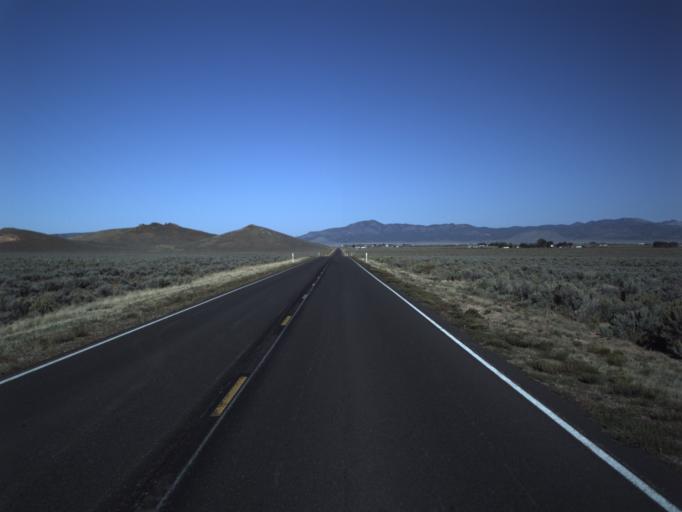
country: US
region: Utah
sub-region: Washington County
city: Enterprise
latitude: 37.7363
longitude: -113.7308
